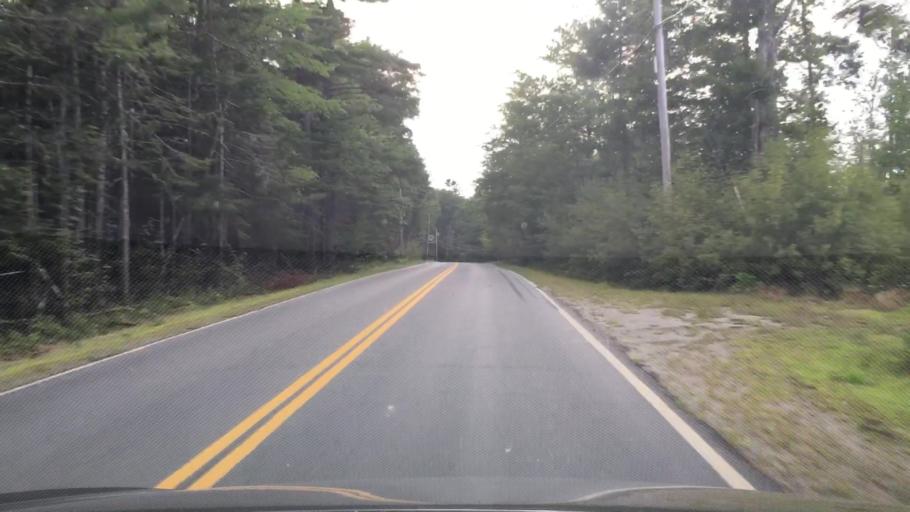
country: US
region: Maine
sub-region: Hancock County
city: Penobscot
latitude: 44.4508
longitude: -68.6905
